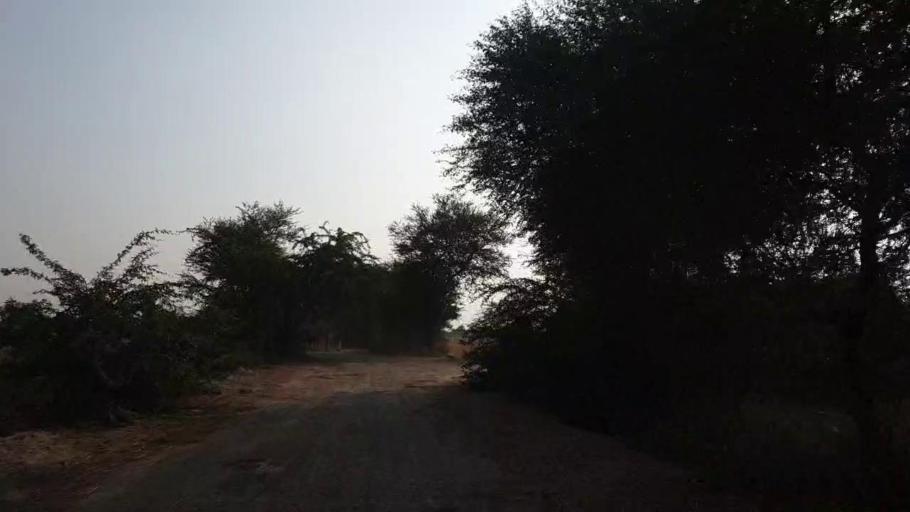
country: PK
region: Sindh
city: Kario
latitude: 24.9005
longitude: 68.5675
